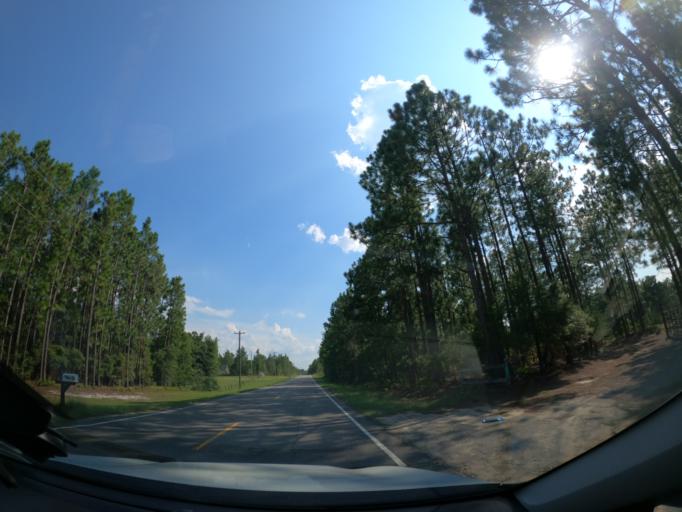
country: US
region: South Carolina
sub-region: Barnwell County
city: Williston
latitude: 33.5351
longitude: -81.4938
